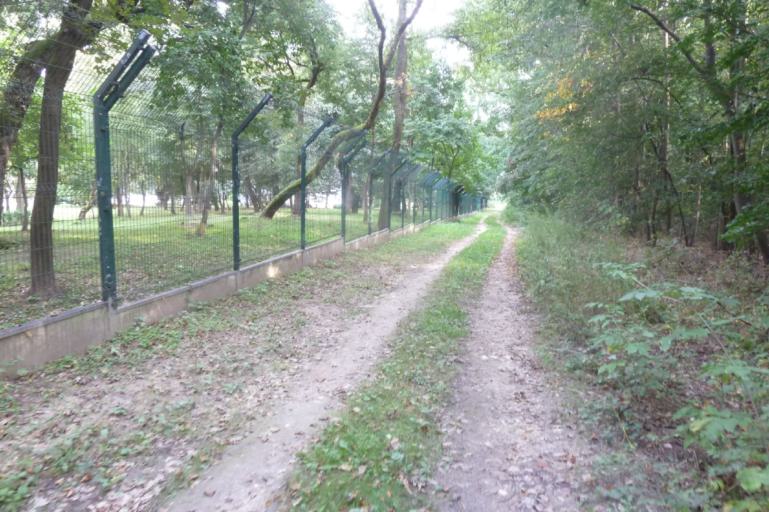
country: HU
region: Pest
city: Godollo
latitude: 47.6017
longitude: 19.3239
